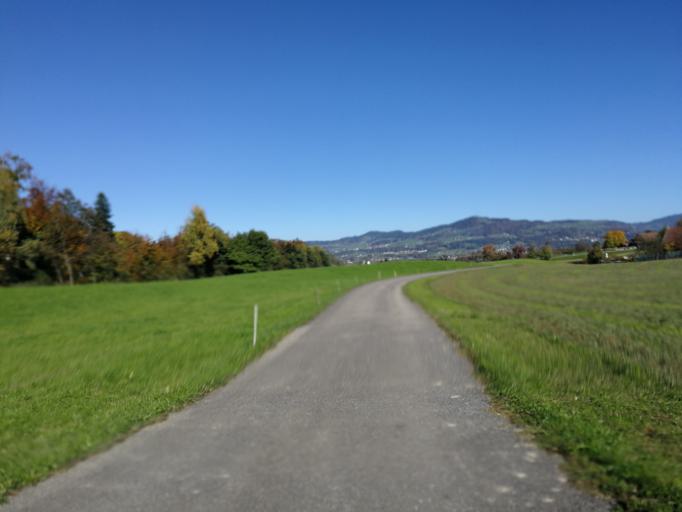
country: CH
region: Zurich
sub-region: Bezirk Hinwil
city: Wolfhausen
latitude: 47.2490
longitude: 8.8089
